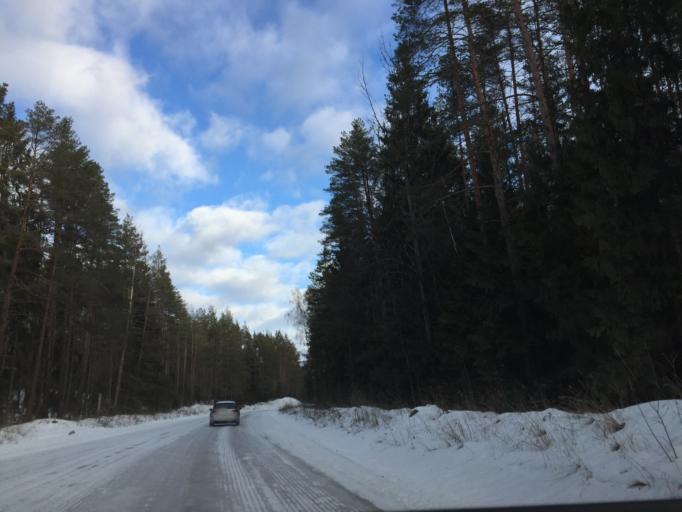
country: LV
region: Ogre
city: Jumprava
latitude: 56.5744
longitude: 24.9388
